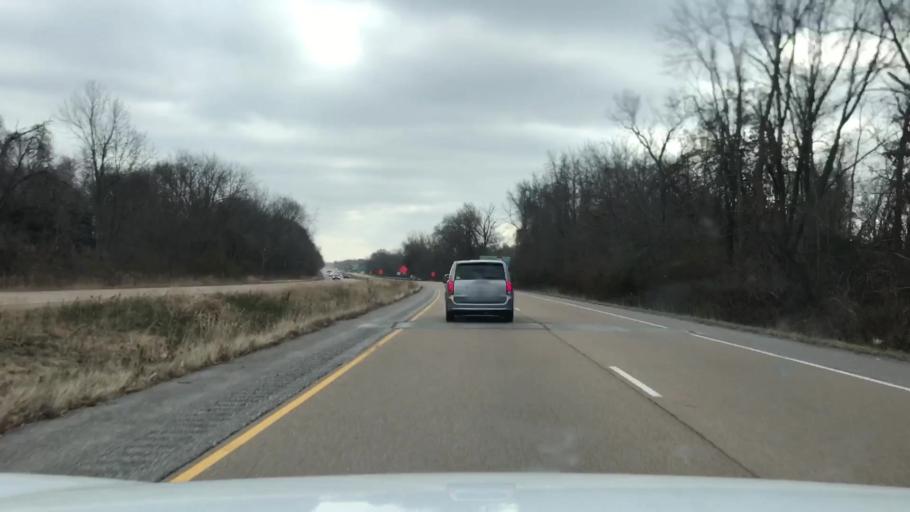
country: US
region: Illinois
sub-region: Saint Clair County
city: Belleville
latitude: 38.5132
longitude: -90.0188
